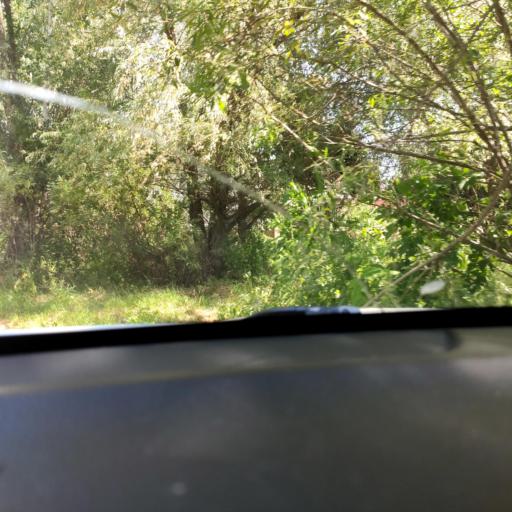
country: RU
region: Tatarstan
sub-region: Gorod Kazan'
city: Kazan
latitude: 55.7724
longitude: 49.2462
